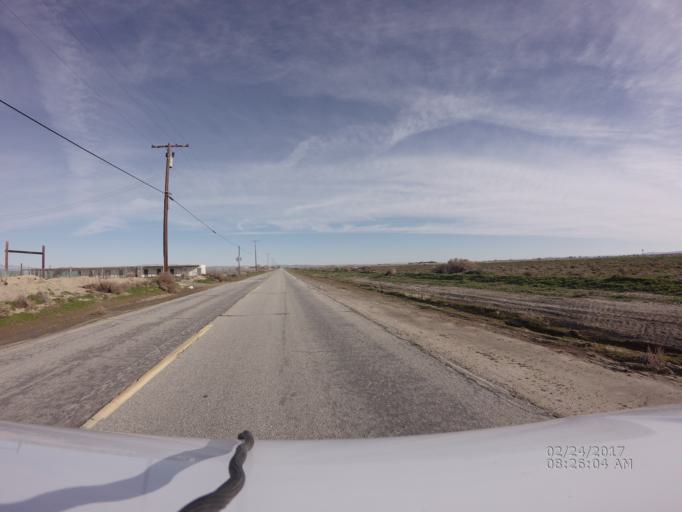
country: US
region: California
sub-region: Los Angeles County
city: Lancaster
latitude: 34.7199
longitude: -118.0234
